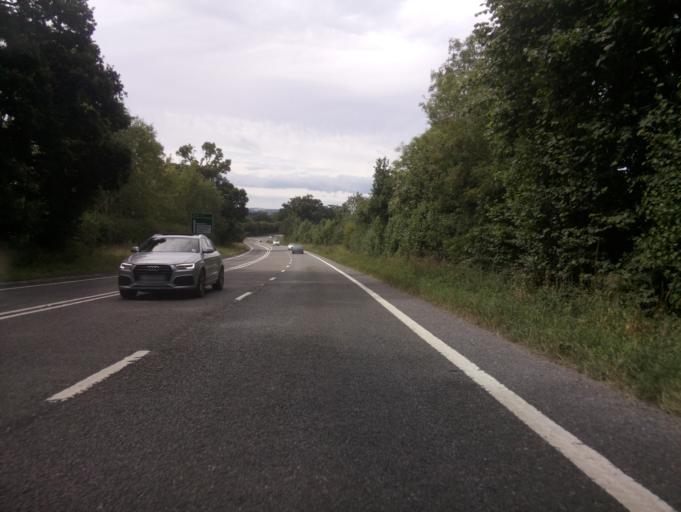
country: GB
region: England
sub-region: Somerset
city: Yeovil
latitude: 50.8580
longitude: -2.5892
